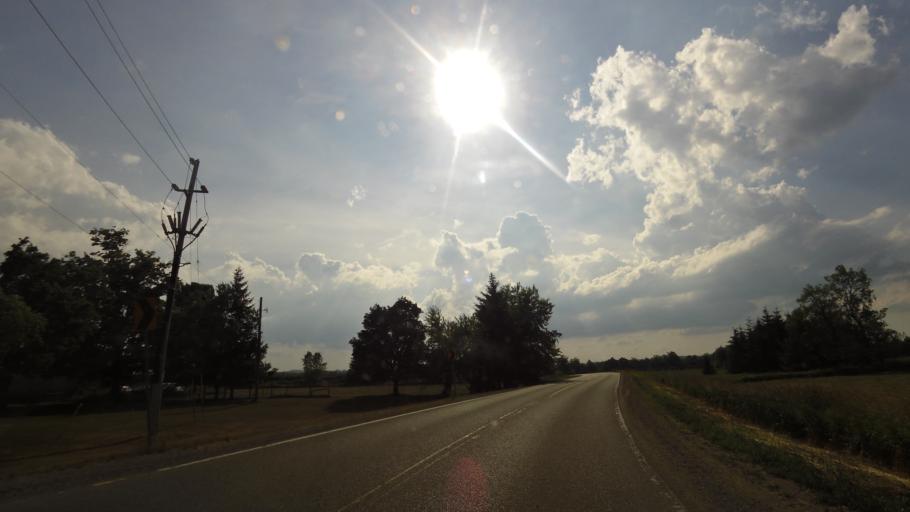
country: CA
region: Ontario
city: Orangeville
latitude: 43.9510
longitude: -80.0789
